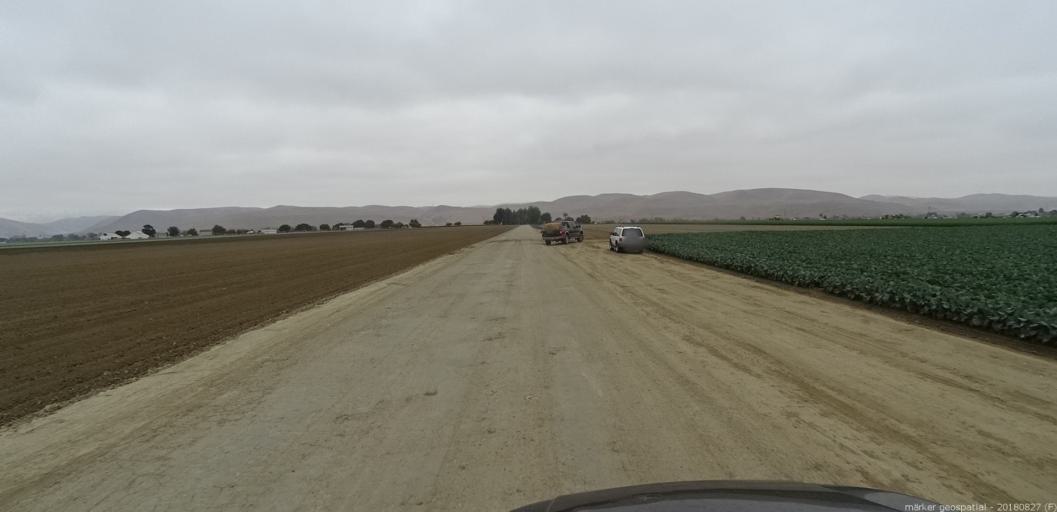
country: US
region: California
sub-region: Monterey County
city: Greenfield
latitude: 36.3205
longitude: -121.2080
